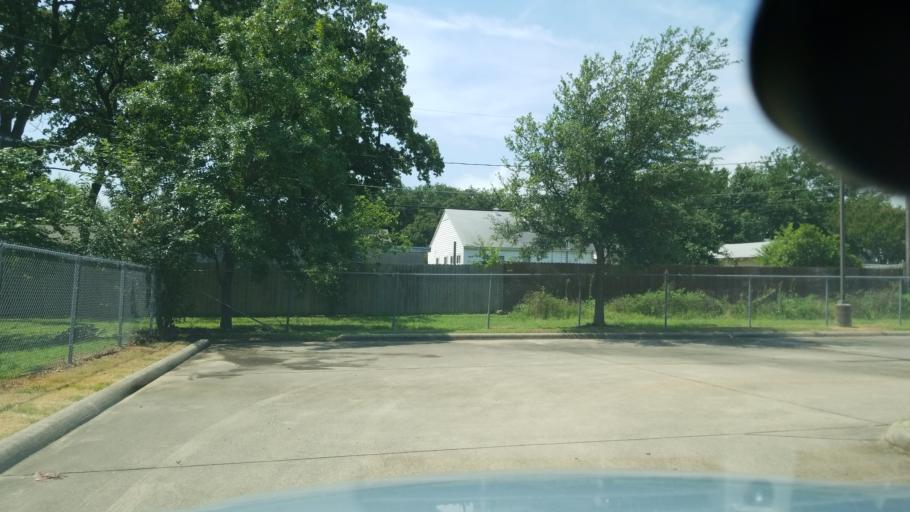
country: US
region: Texas
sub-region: Dallas County
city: Irving
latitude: 32.8319
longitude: -96.9424
